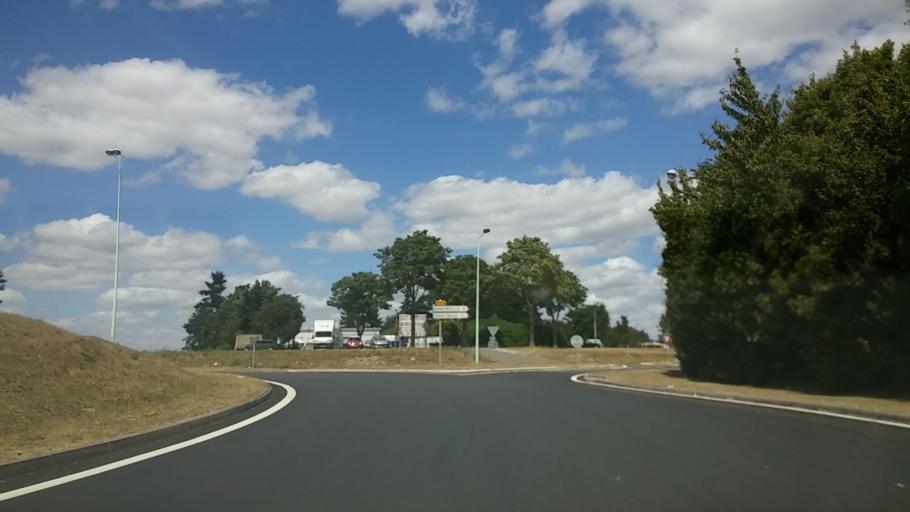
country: FR
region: Ile-de-France
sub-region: Departement des Yvelines
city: Houdan
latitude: 48.7921
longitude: 1.6302
